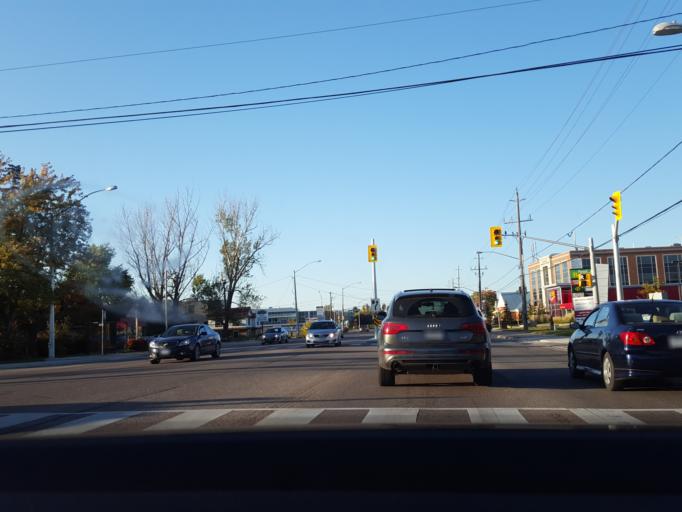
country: CA
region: Ontario
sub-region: York
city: Richmond Hill
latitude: 43.9500
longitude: -79.4559
